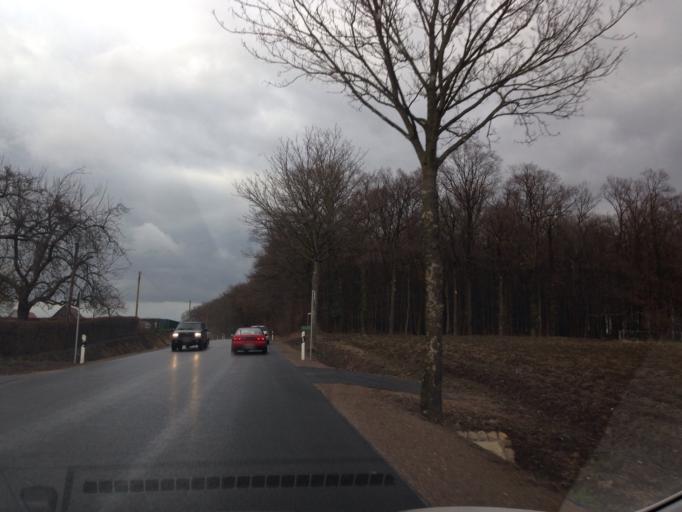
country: DE
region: North Rhine-Westphalia
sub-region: Regierungsbezirk Munster
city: Nordkirchen
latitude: 51.7740
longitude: 7.5453
